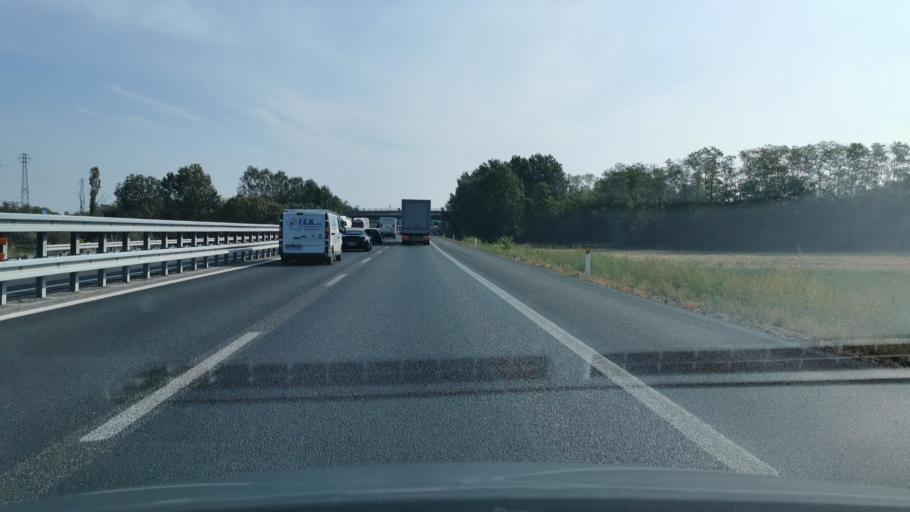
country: IT
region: Lombardy
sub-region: Provincia di Pavia
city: Broni
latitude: 45.0778
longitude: 9.2700
